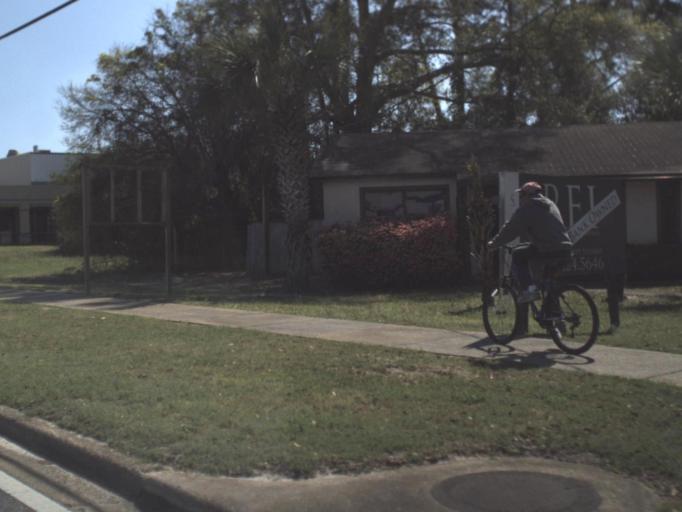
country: US
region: Florida
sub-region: Okaloosa County
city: Fort Walton Beach
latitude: 30.4175
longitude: -86.6138
